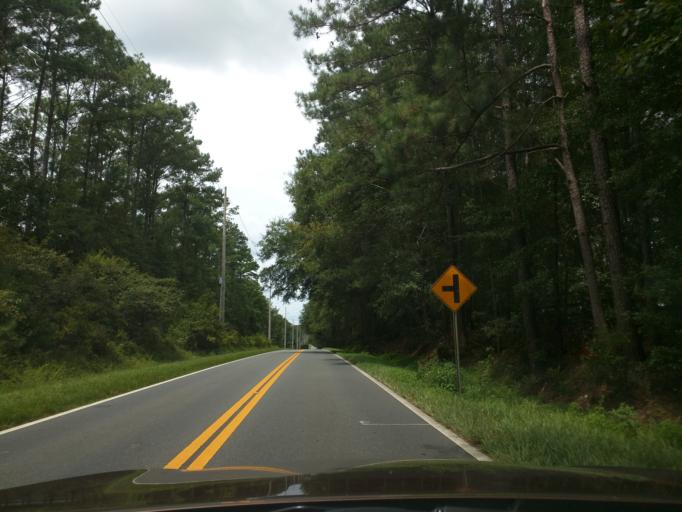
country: US
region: Florida
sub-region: Leon County
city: Tallahassee
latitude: 30.5602
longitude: -84.1959
